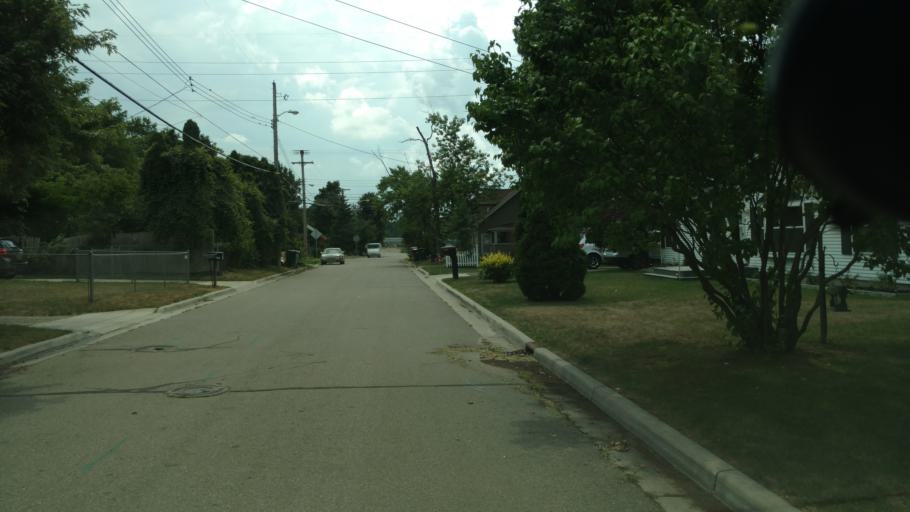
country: US
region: Michigan
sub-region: Ingham County
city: Lansing
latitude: 42.7621
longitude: -84.5589
